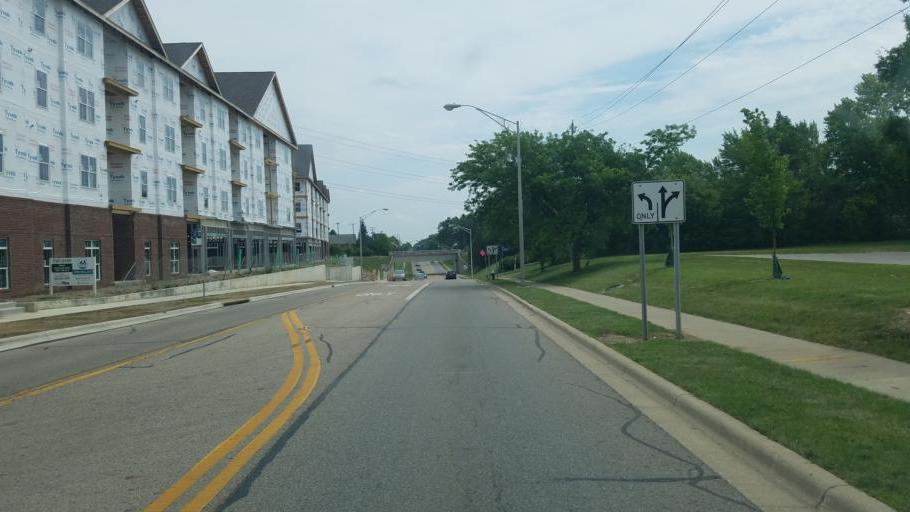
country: US
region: Ohio
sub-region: Franklin County
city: Hilliard
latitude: 40.0301
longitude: -83.1575
